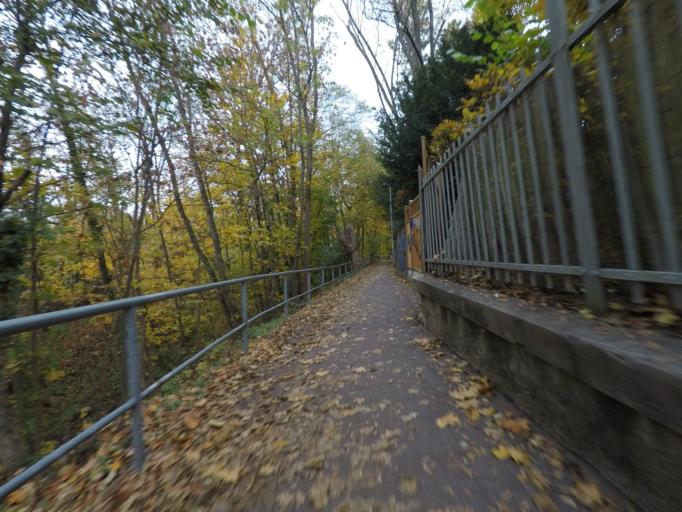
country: DE
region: Baden-Wuerttemberg
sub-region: Tuebingen Region
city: Reutlingen
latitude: 48.4975
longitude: 9.2186
